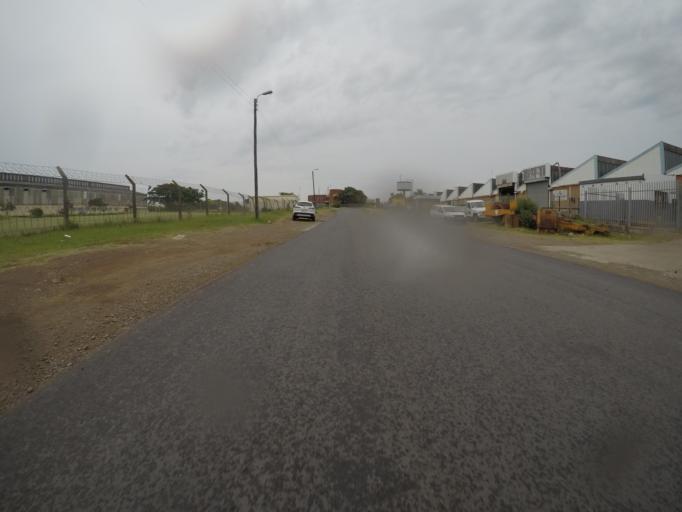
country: ZA
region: Eastern Cape
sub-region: Buffalo City Metropolitan Municipality
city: East London
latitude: -32.9738
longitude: 27.8228
